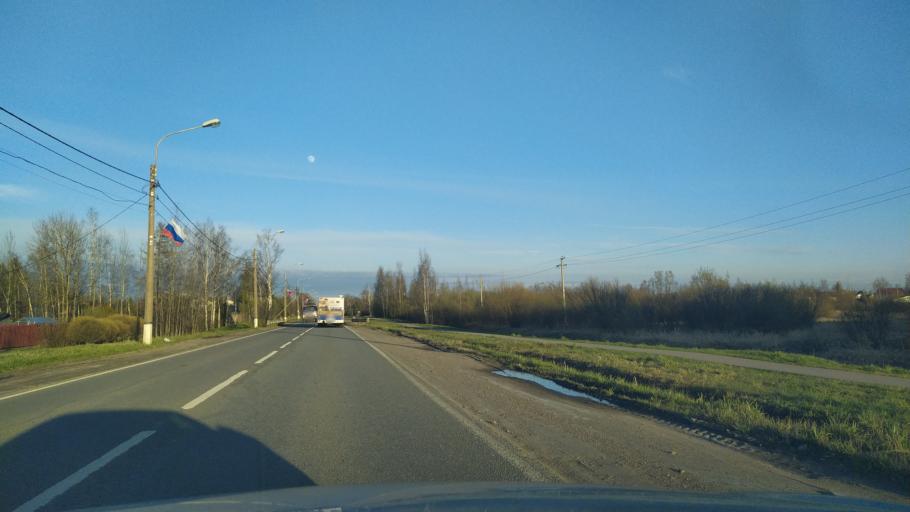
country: RU
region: St.-Petersburg
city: Aleksandrovskaya
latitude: 59.7390
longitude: 30.3249
